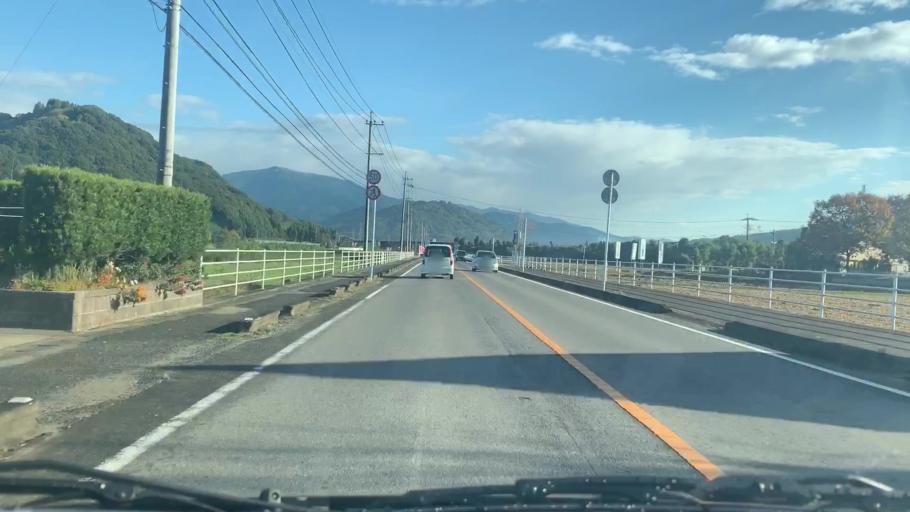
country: JP
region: Saga Prefecture
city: Takeocho-takeo
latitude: 33.2539
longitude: 130.0761
